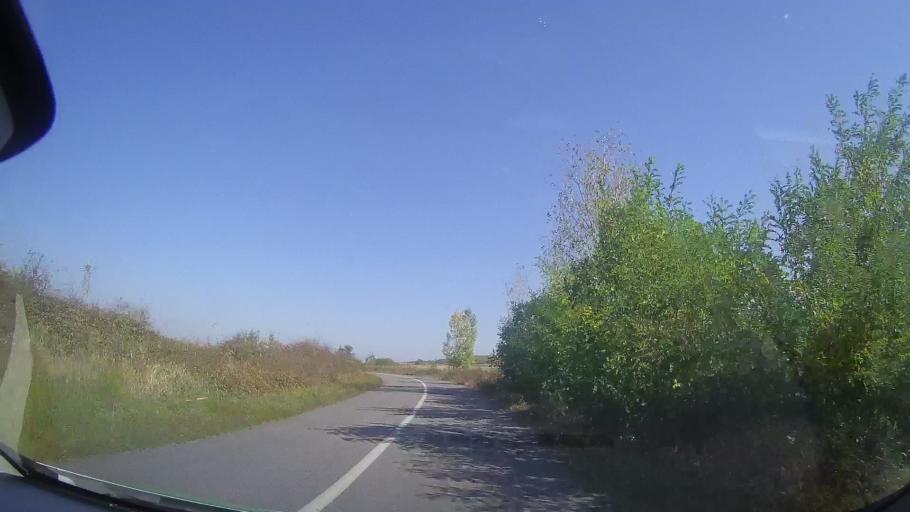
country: RO
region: Timis
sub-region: Comuna Balint
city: Balint
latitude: 45.8265
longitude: 21.8517
